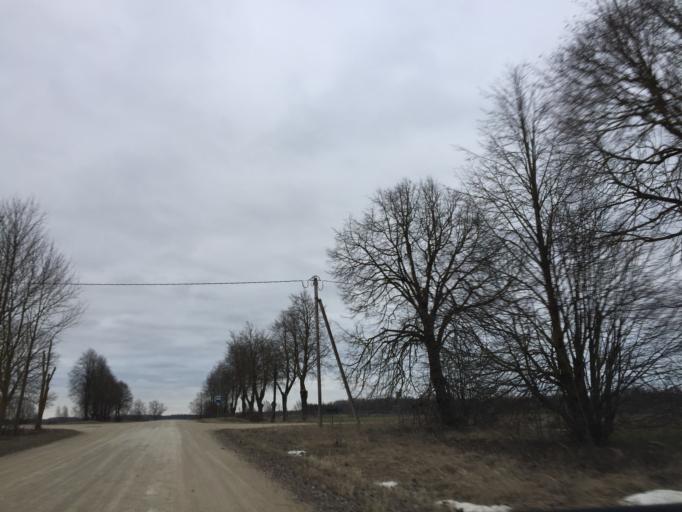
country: LT
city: Zagare
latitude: 56.3138
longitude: 23.2482
